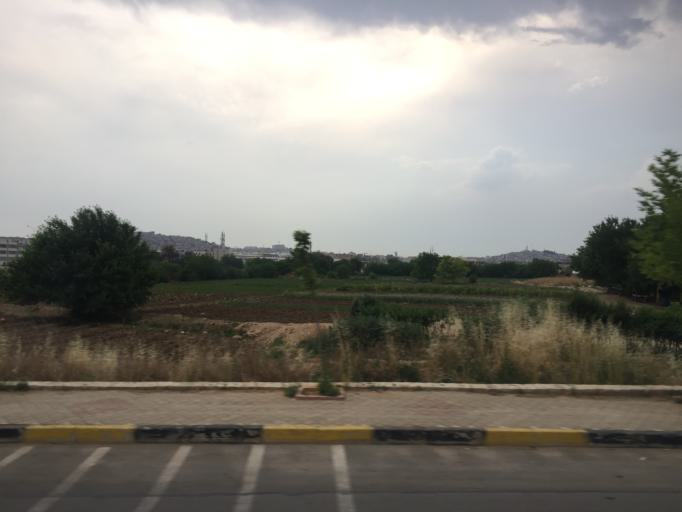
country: TR
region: Gaziantep
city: Gaziantep
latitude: 37.0580
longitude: 37.4157
